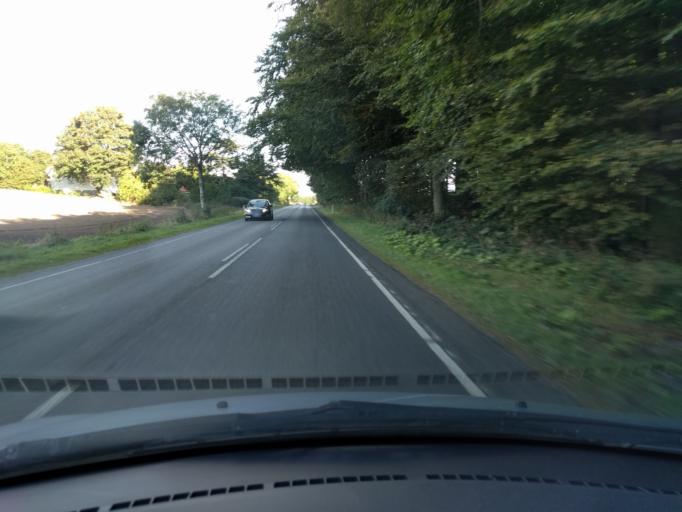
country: DK
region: South Denmark
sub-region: Assens Kommune
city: Glamsbjerg
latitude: 55.2688
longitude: 10.0883
